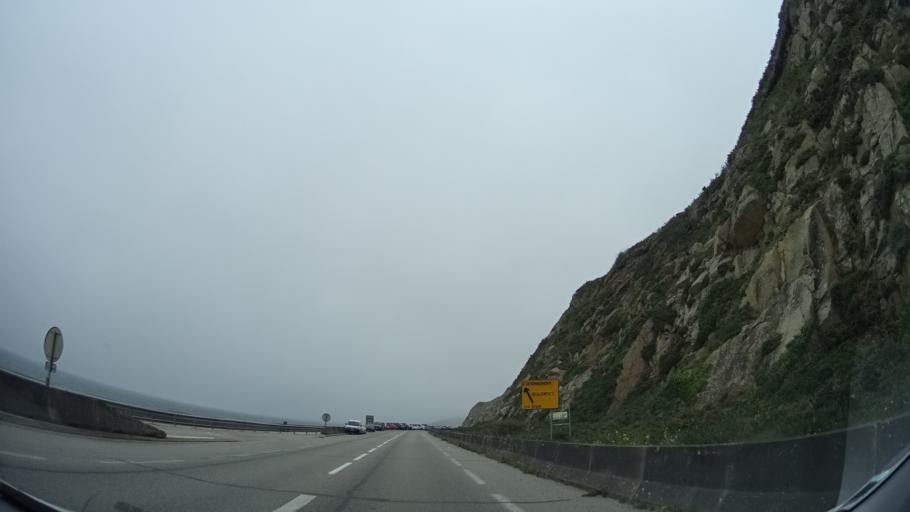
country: FR
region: Lower Normandy
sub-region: Departement de la Manche
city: Flamanville
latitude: 49.5459
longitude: -1.8718
